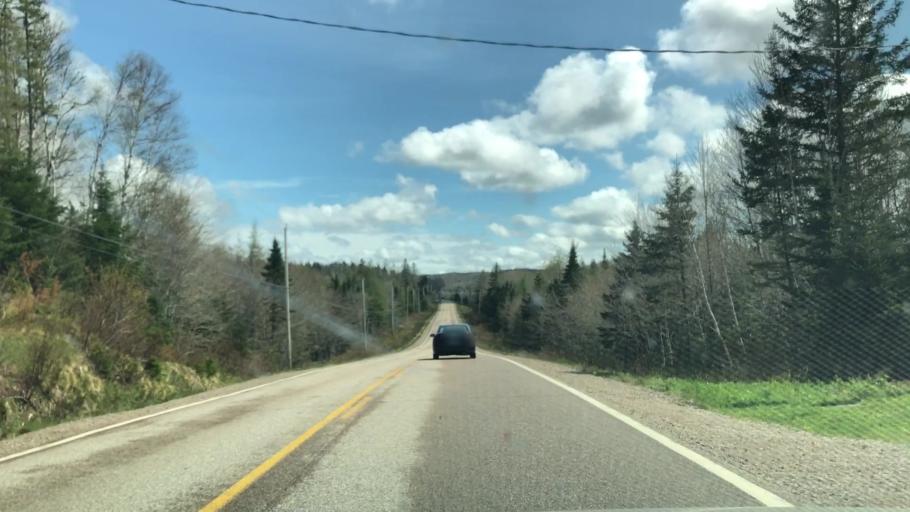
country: CA
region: Nova Scotia
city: Antigonish
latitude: 45.2069
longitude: -62.0038
